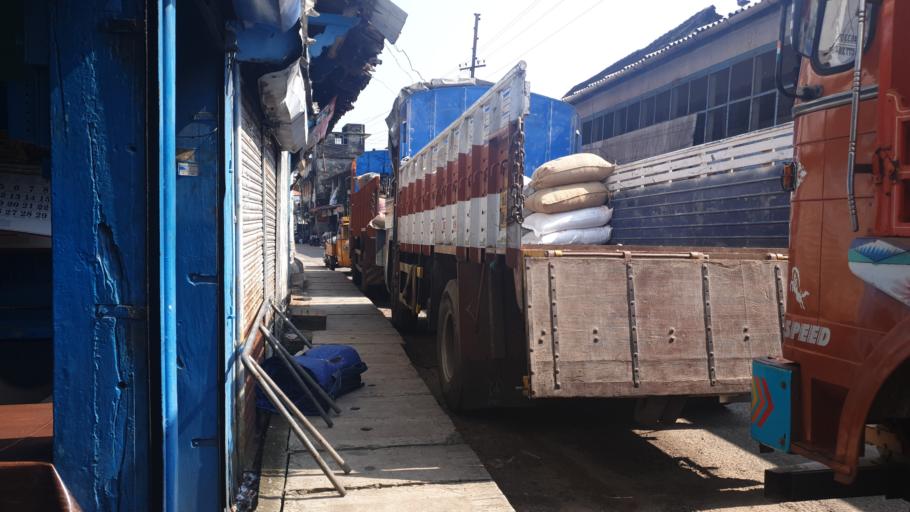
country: IN
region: Kerala
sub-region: Ernakulam
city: Cochin
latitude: 9.9657
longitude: 76.2542
